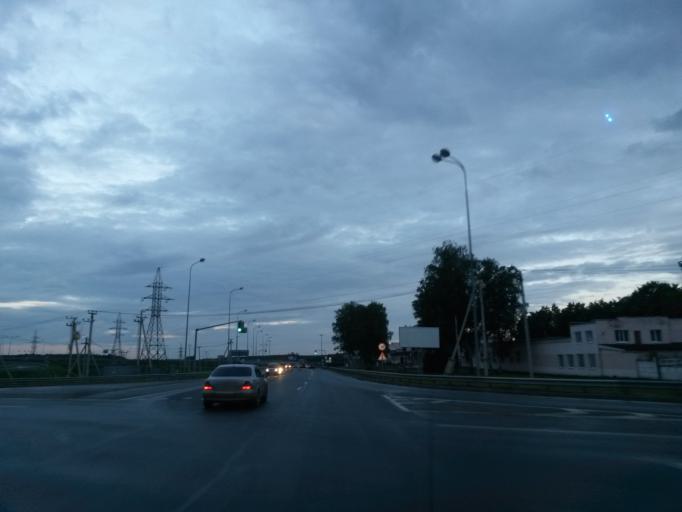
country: RU
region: Jaroslavl
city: Yaroslavl
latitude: 57.6880
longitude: 39.8978
